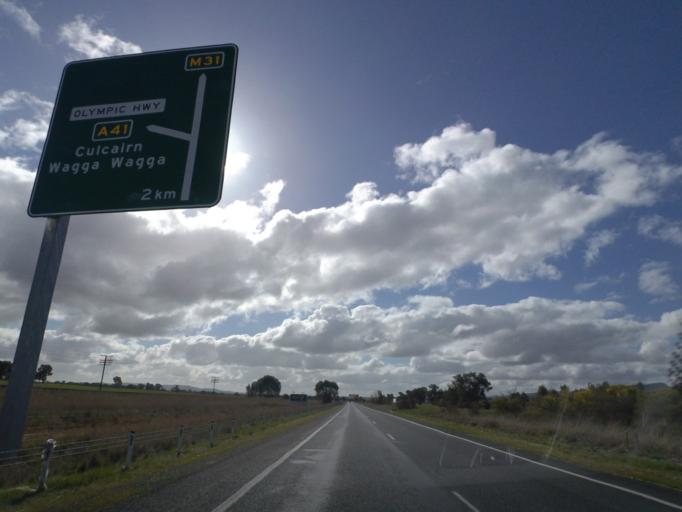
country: AU
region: New South Wales
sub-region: Greater Hume Shire
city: Jindera
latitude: -35.9483
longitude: 147.0036
